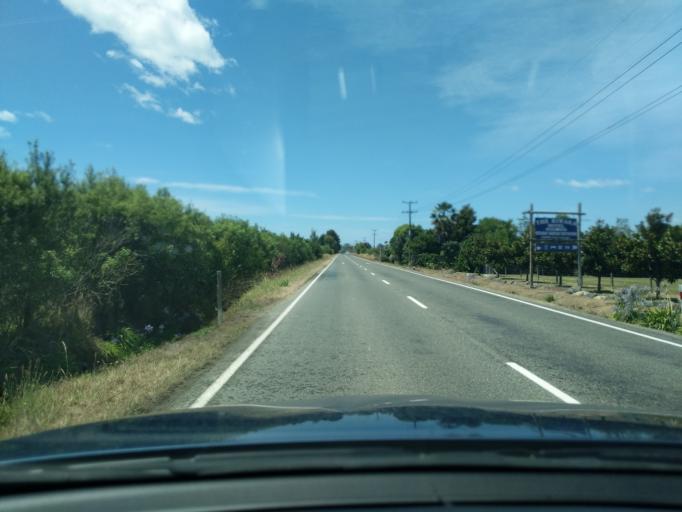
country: NZ
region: Tasman
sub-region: Tasman District
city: Motueka
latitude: -41.0700
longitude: 172.9910
